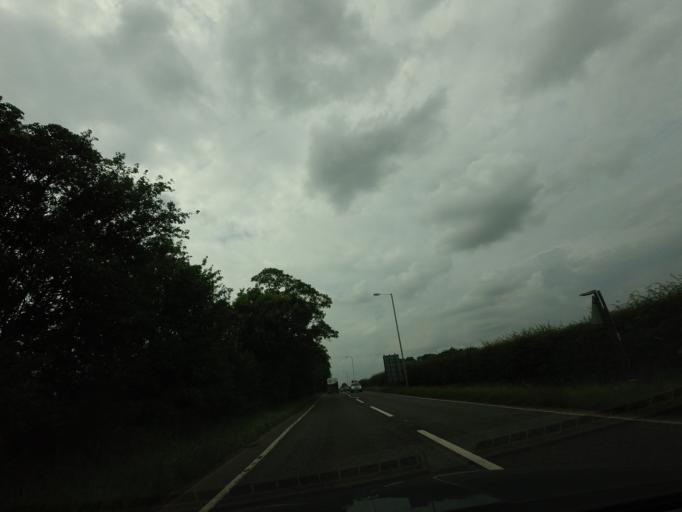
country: GB
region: England
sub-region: Shropshire
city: Tong
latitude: 52.6679
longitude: -2.3083
